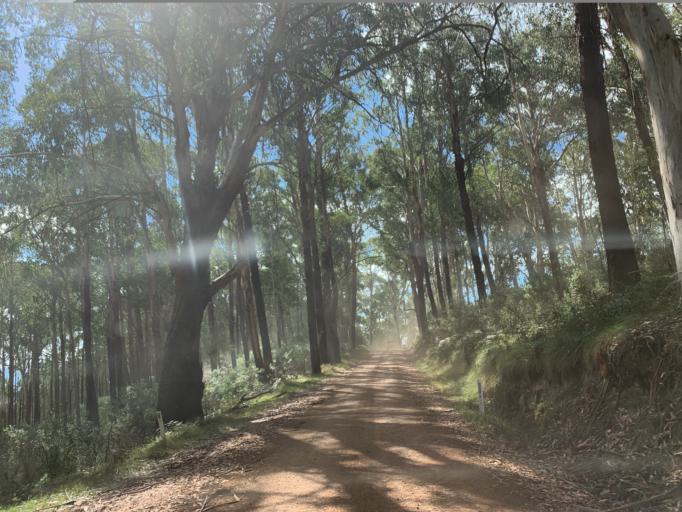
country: AU
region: Victoria
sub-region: Mansfield
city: Mansfield
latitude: -37.0922
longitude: 146.5417
